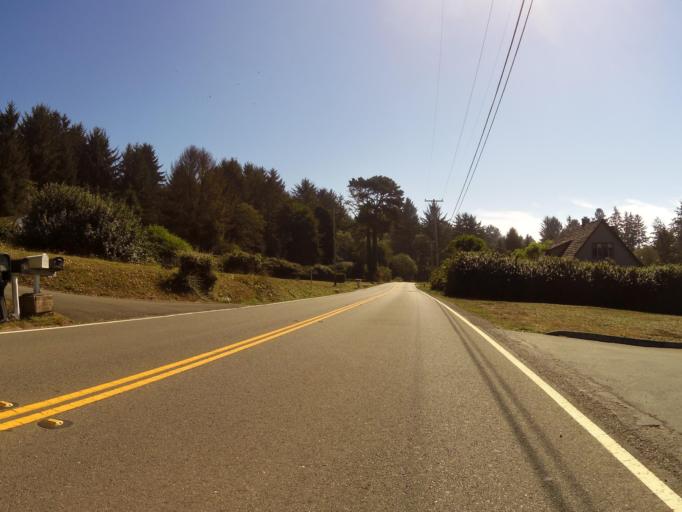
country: US
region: Oregon
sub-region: Curry County
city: Harbor
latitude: 41.9613
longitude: -124.1990
